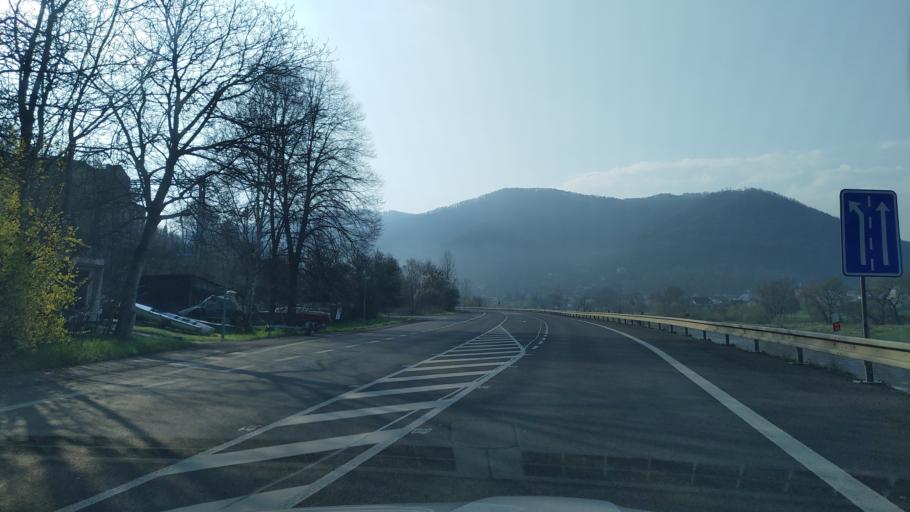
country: CZ
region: Ustecky
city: Velke Brezno
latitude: 50.6720
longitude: 14.1364
